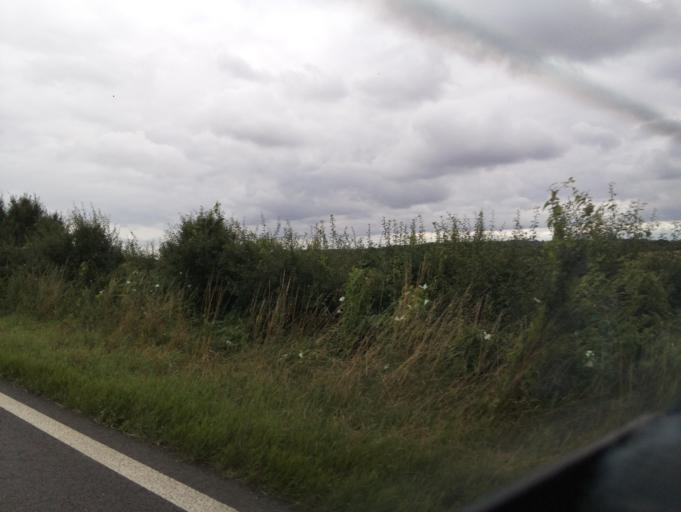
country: GB
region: England
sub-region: Lincolnshire
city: Long Bennington
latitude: 52.9345
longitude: -0.7562
